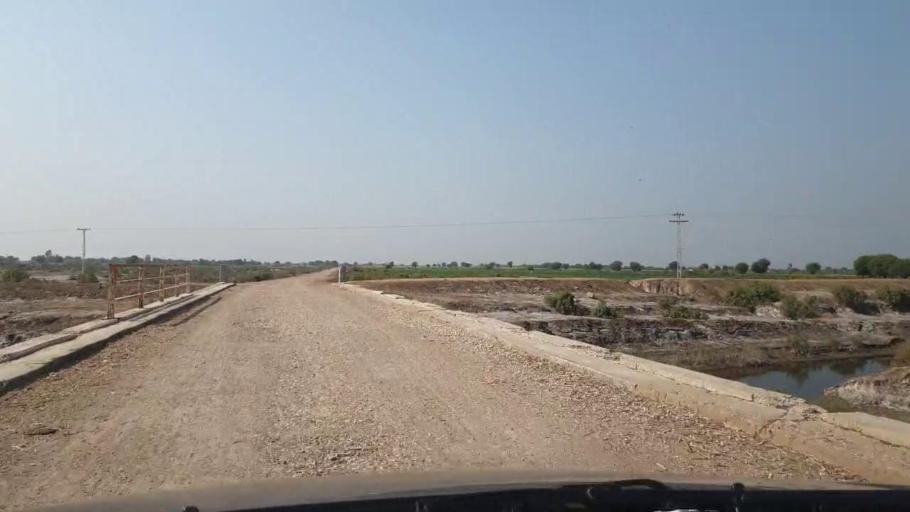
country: PK
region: Sindh
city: Jhol
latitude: 25.8922
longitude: 68.9580
